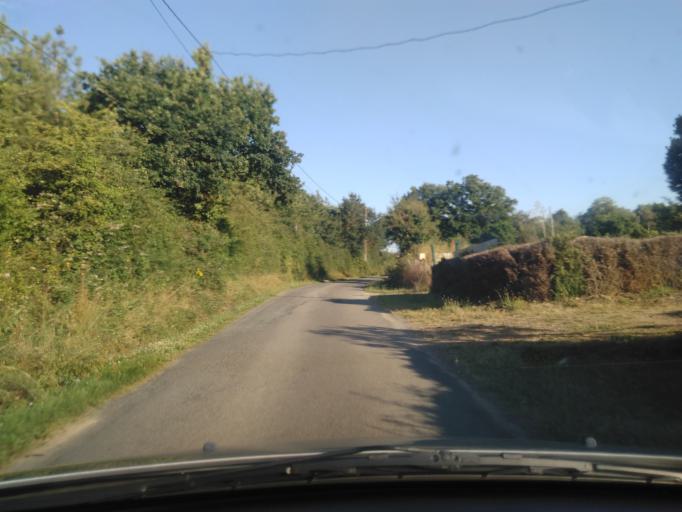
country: FR
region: Pays de la Loire
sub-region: Departement de la Vendee
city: La Roche-sur-Yon
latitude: 46.7032
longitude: -1.4103
